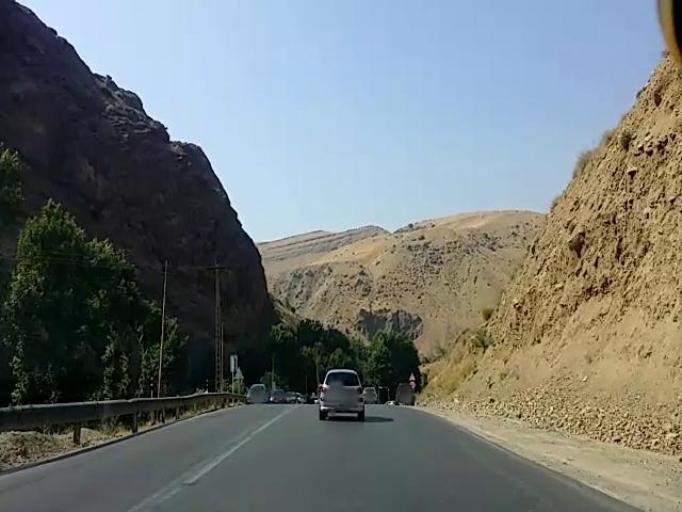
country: IR
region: Alborz
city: Karaj
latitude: 35.9099
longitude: 51.0434
